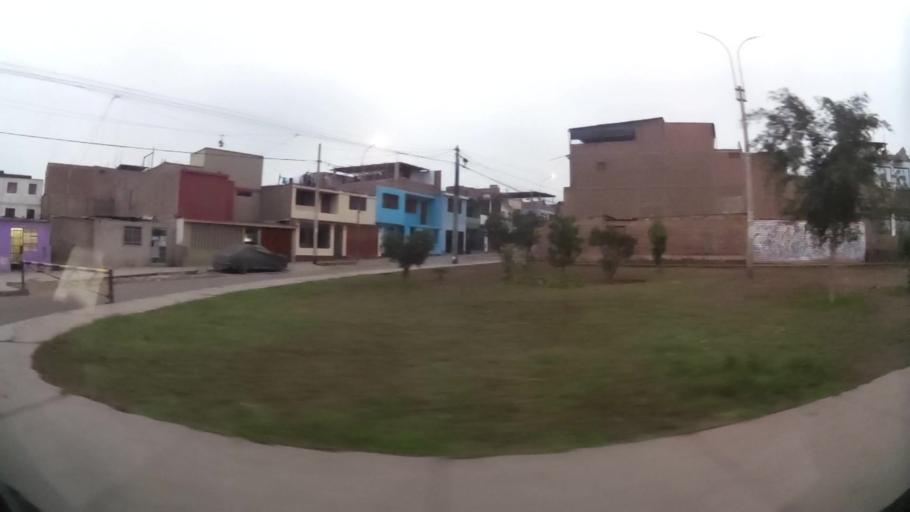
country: PE
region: Lima
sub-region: Lima
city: Surco
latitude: -12.1468
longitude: -76.9727
